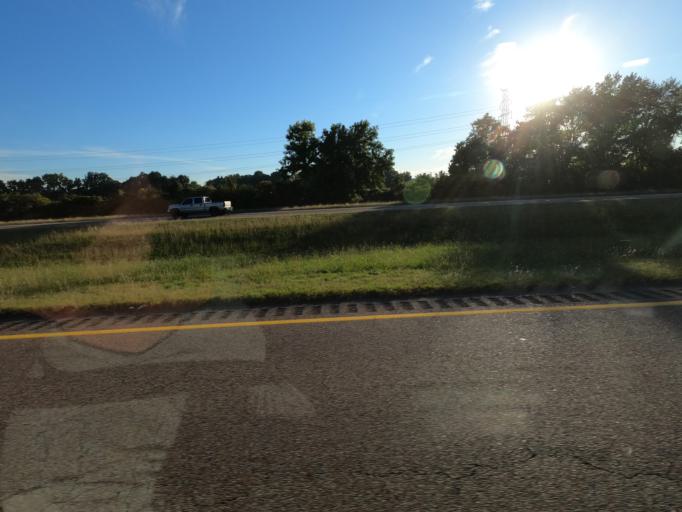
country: US
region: Tennessee
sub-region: Shelby County
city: Millington
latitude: 35.3235
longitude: -89.8804
